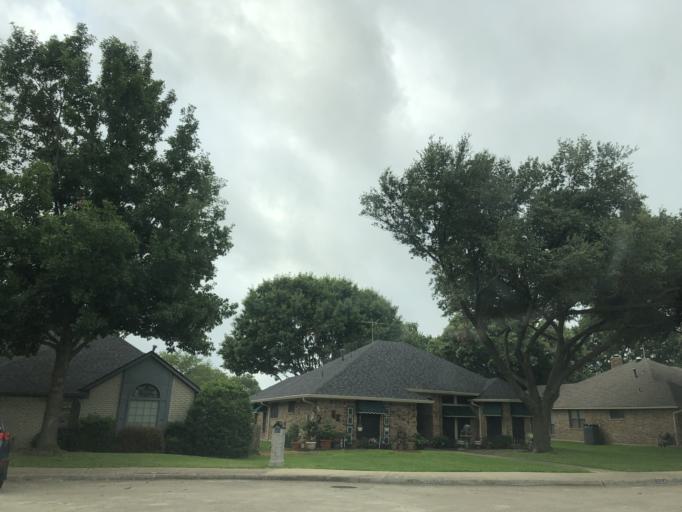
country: US
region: Texas
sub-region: Dallas County
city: Garland
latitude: 32.8363
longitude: -96.6447
